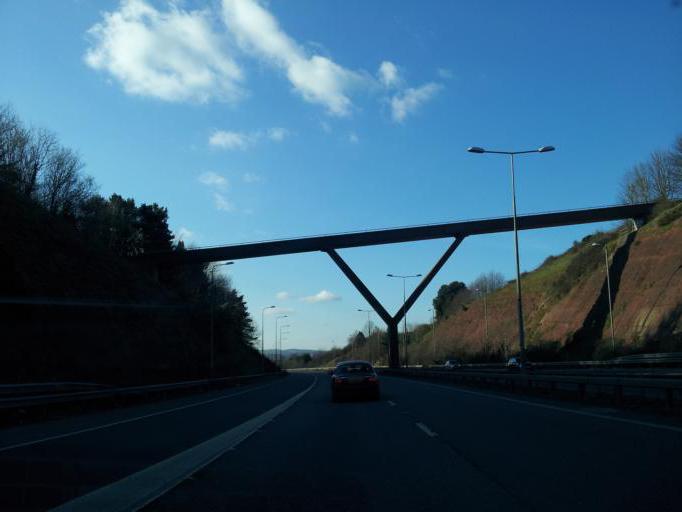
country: GB
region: England
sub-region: Devon
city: Exminster
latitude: 50.6820
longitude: -3.5187
